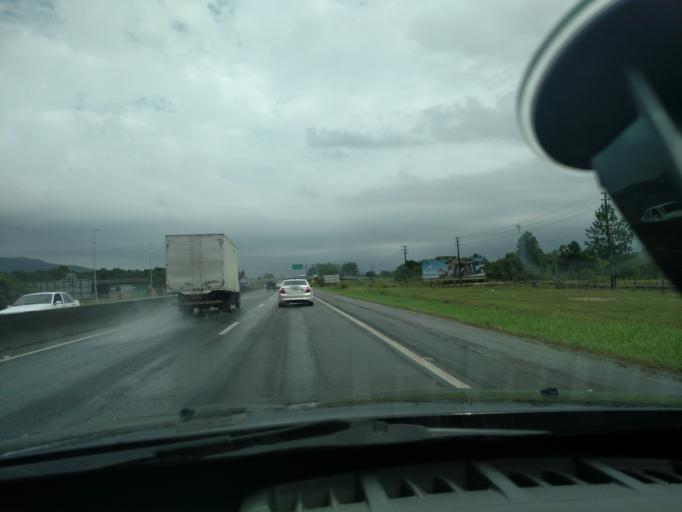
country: BR
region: Santa Catarina
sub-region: Porto Belo
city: Porto Belo
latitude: -27.1566
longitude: -48.6110
